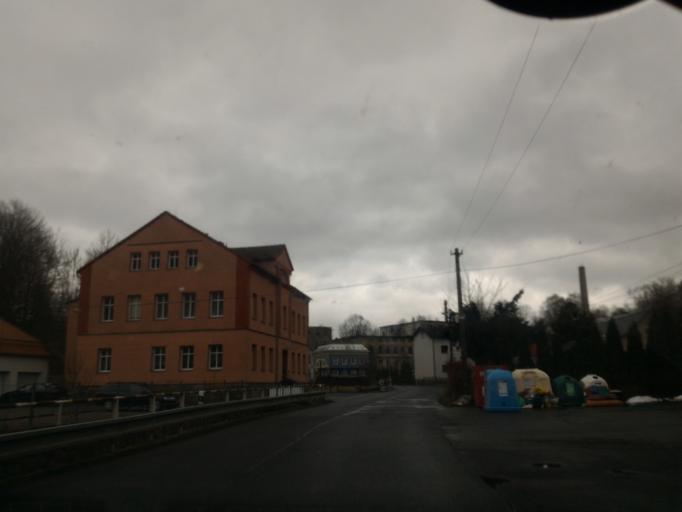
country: CZ
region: Ustecky
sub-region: Okres Decin
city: Krasna Lipa
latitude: 50.9160
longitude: 14.4978
